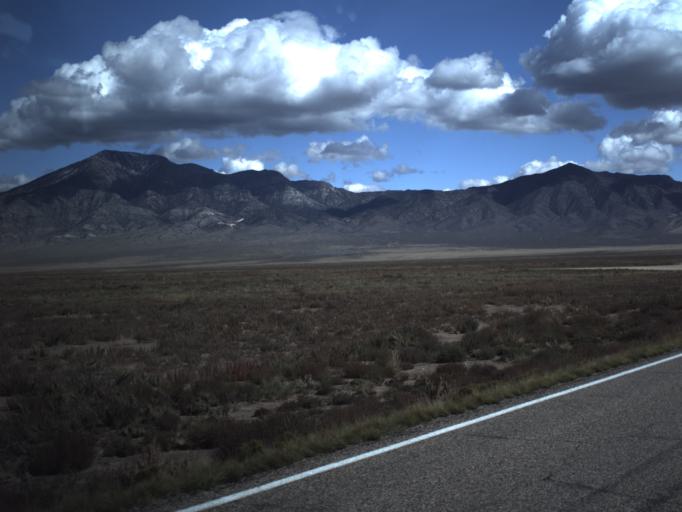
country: US
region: Utah
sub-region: Beaver County
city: Milford
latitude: 38.4697
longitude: -113.4045
